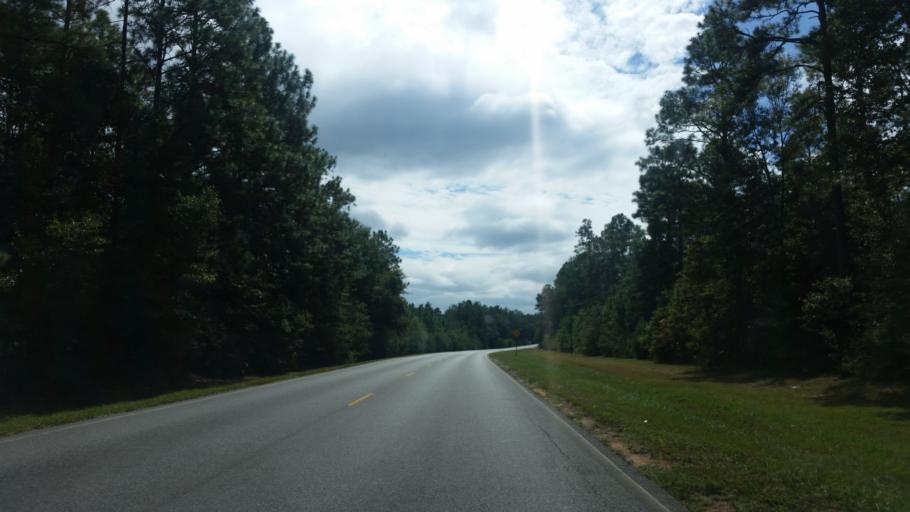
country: US
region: Florida
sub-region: Santa Rosa County
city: Point Baker
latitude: 30.7521
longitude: -86.9432
